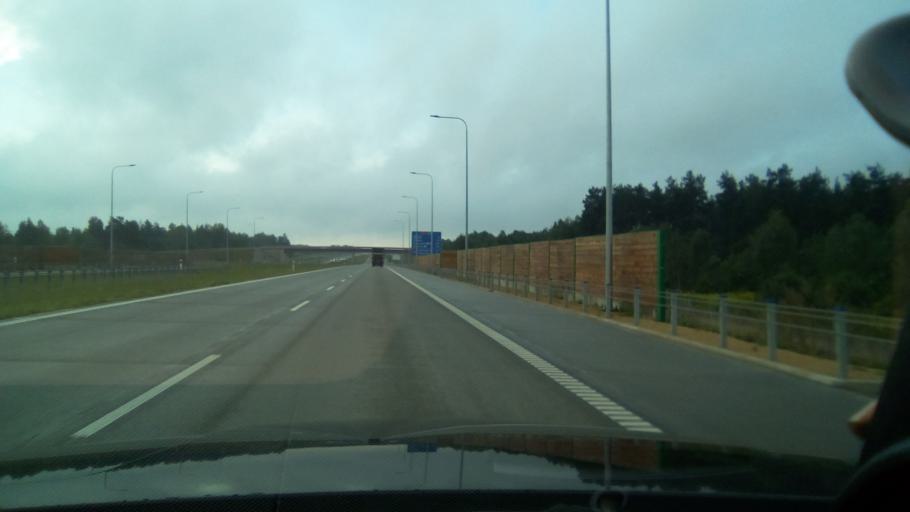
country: PL
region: Silesian Voivodeship
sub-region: Powiat czestochowski
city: Blachownia
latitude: 50.7744
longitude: 19.0090
